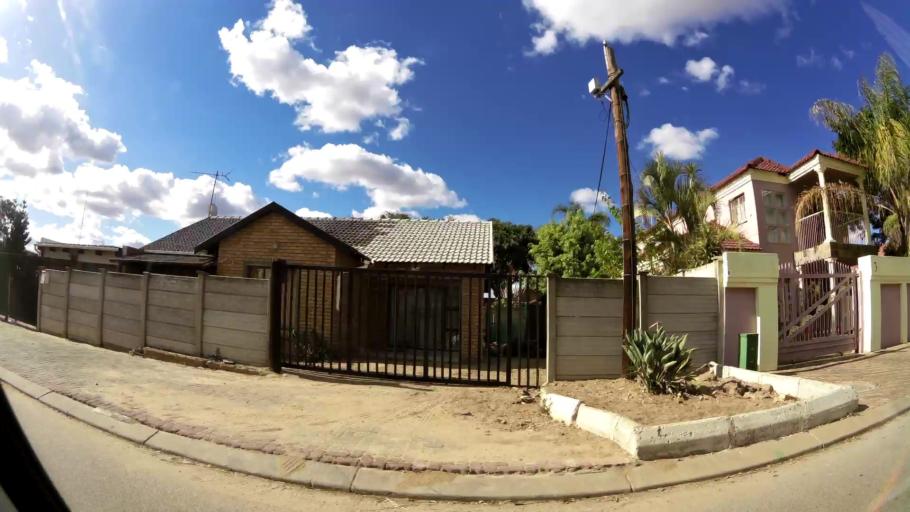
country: ZA
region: Limpopo
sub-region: Capricorn District Municipality
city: Polokwane
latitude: -23.8843
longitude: 29.4708
